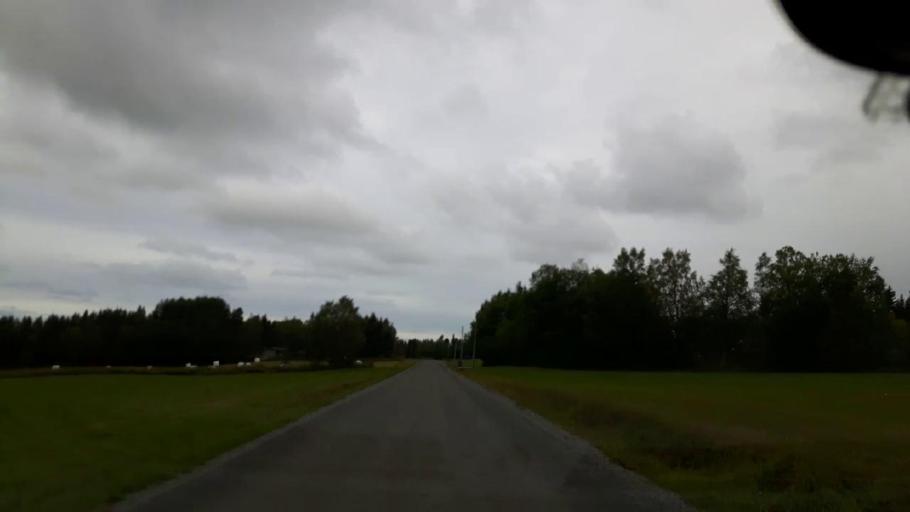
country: SE
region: Jaemtland
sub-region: OEstersunds Kommun
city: Ostersund
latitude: 63.0911
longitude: 14.5545
